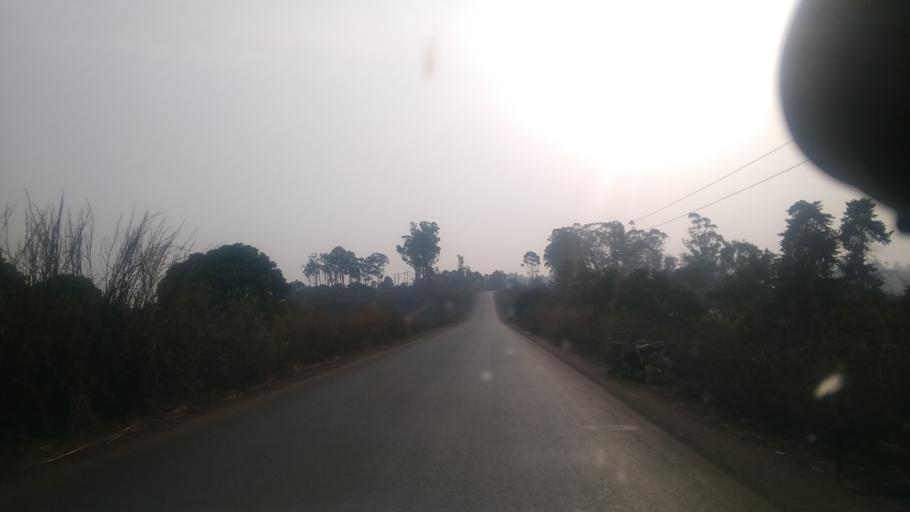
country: CM
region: West
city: Bangangte
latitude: 5.1622
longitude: 10.5002
